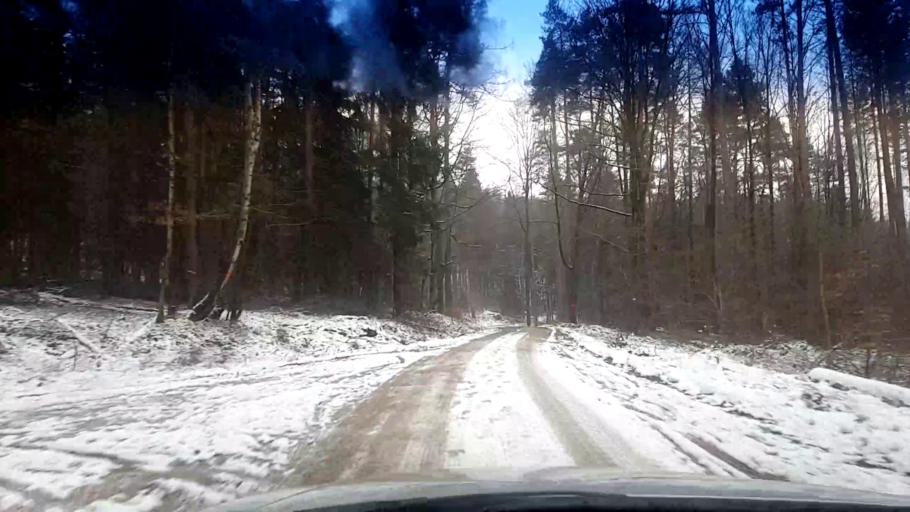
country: DE
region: Bavaria
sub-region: Upper Franconia
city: Gundelsheim
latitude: 49.9609
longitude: 10.9179
